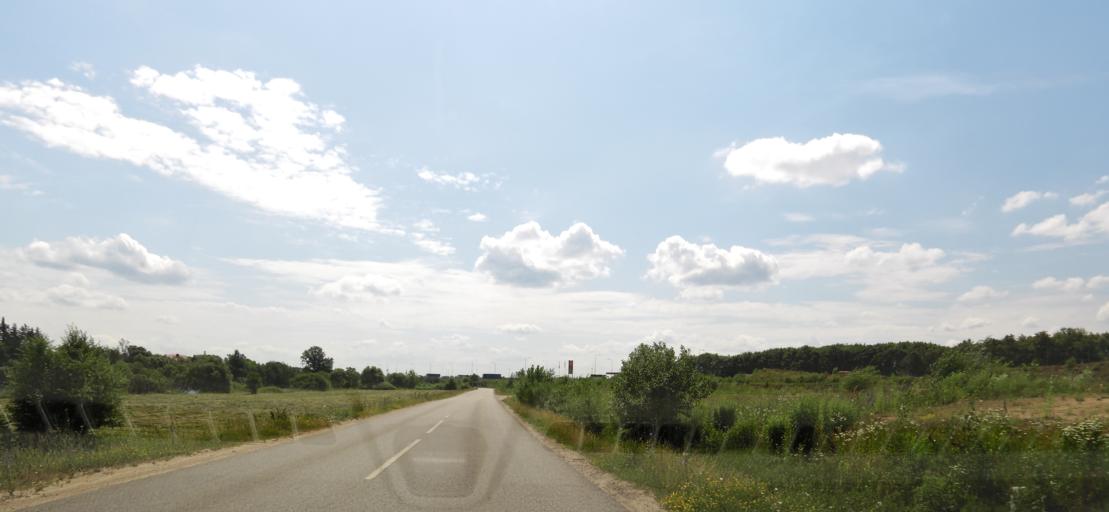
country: LT
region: Vilnius County
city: Pasilaiciai
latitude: 54.7633
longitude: 25.2035
